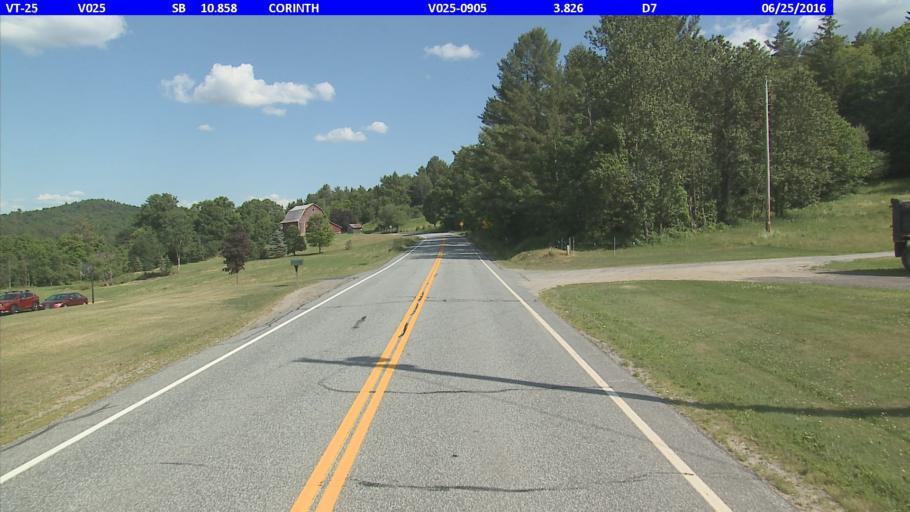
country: US
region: New Hampshire
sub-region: Grafton County
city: Haverhill
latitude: 44.0767
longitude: -72.2588
